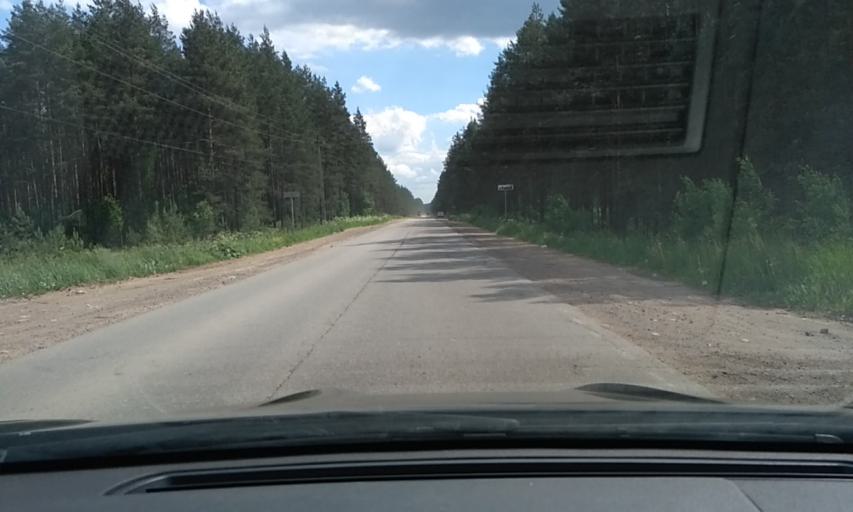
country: RU
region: Leningrad
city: Imeni Sverdlova
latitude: 59.8552
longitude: 30.6745
